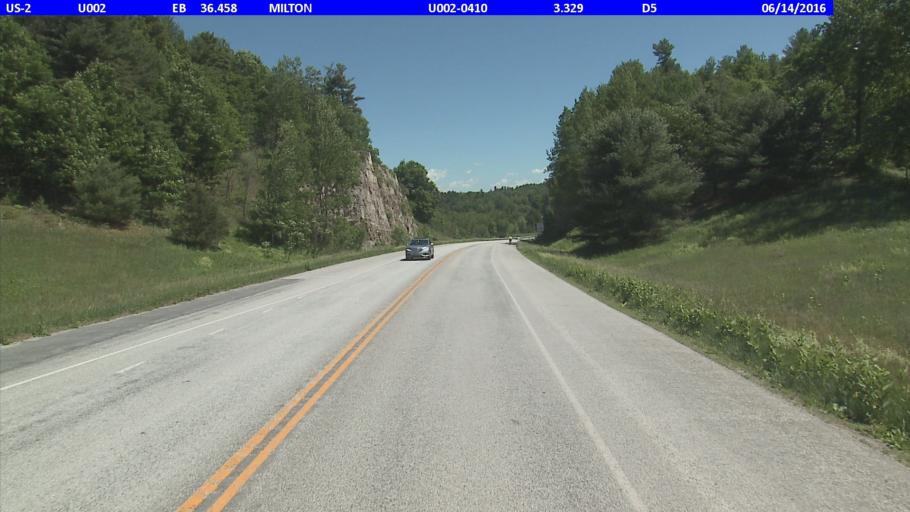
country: US
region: Vermont
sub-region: Chittenden County
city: Colchester
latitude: 44.6083
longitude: -73.2075
